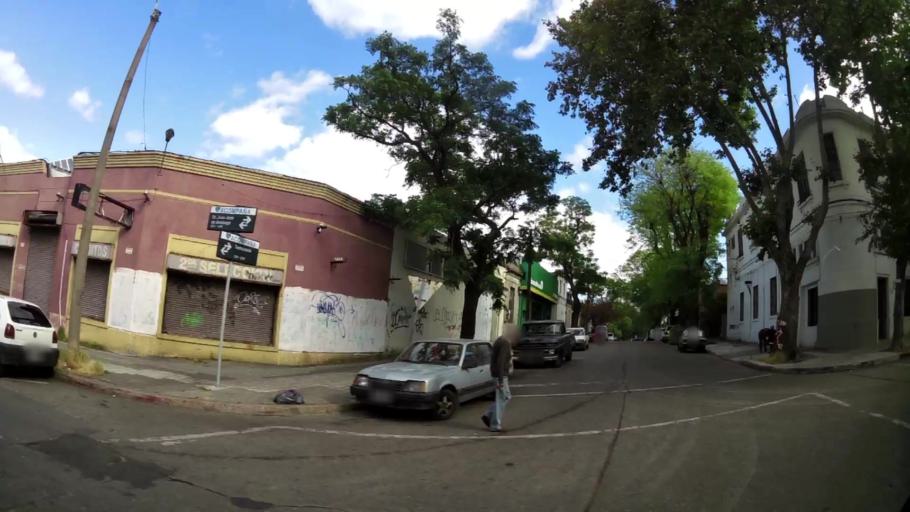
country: UY
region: Montevideo
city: Montevideo
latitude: -34.8865
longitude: -56.1772
